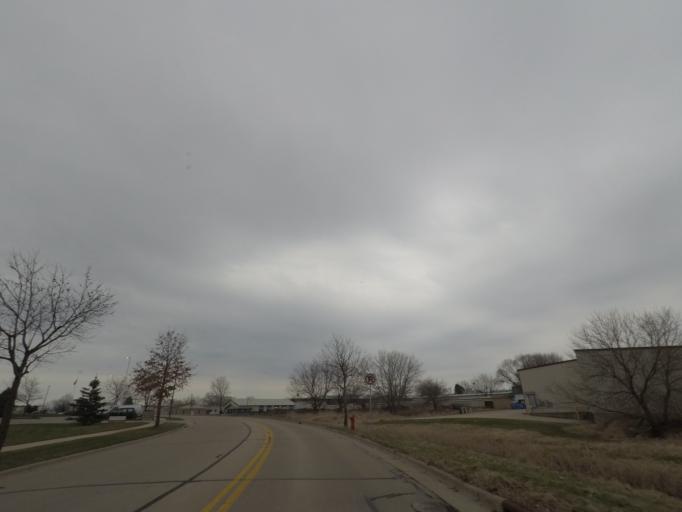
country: US
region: Wisconsin
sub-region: Dane County
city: Middleton
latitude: 43.1035
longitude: -89.5380
